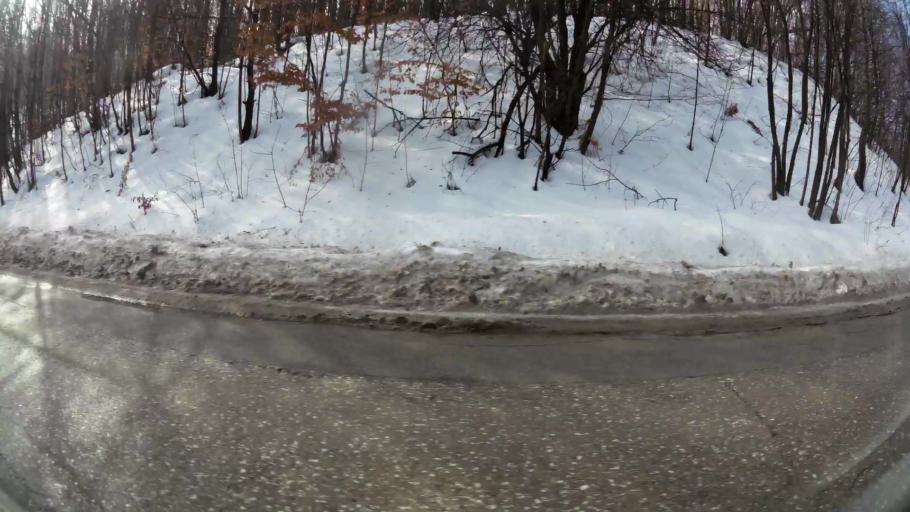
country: BG
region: Sofiya
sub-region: Obshtina Bozhurishte
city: Bozhurishte
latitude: 42.6420
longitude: 23.2183
